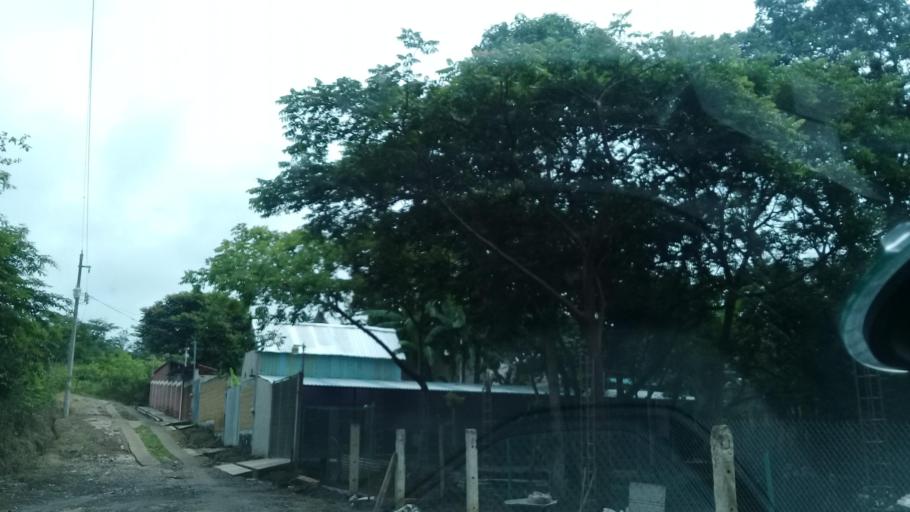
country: MX
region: Veracruz
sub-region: Emiliano Zapata
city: Jacarandas
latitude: 19.4782
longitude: -96.8514
